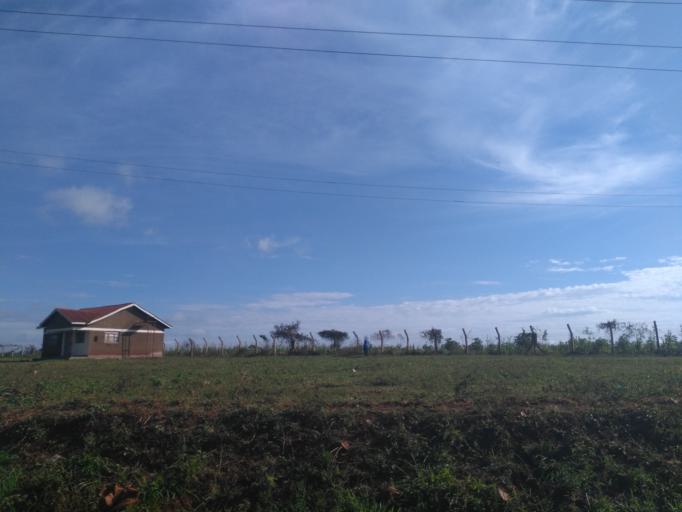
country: UG
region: Eastern Region
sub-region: Jinja District
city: Jinja
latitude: 0.4520
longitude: 33.1911
